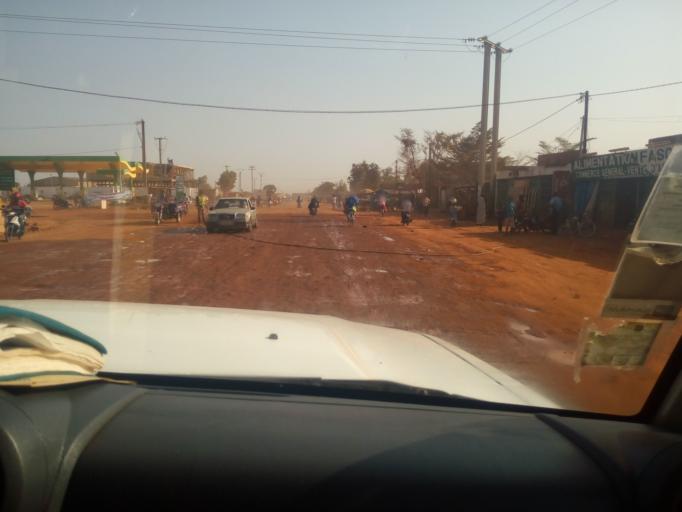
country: BF
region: Centre
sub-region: Kadiogo Province
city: Ouagadougou
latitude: 12.4177
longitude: -1.4729
